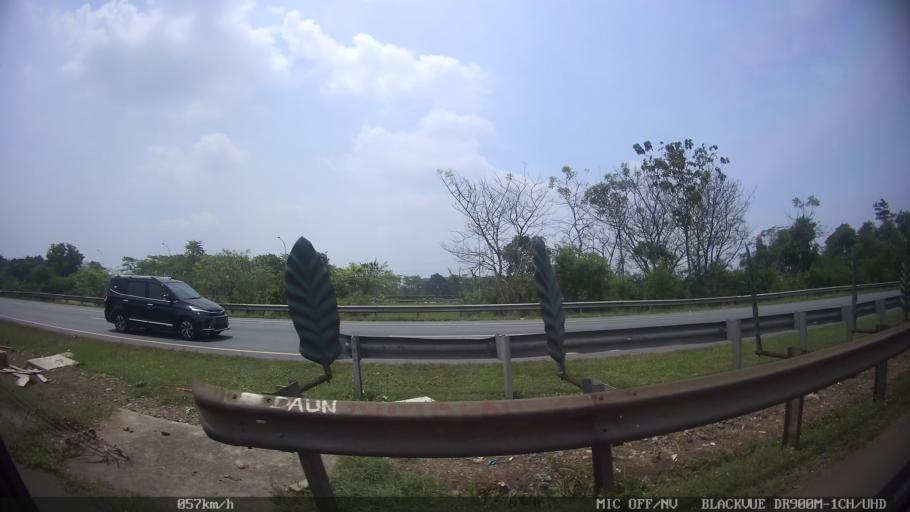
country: ID
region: West Java
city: Kresek
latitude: -6.1446
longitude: 106.2924
